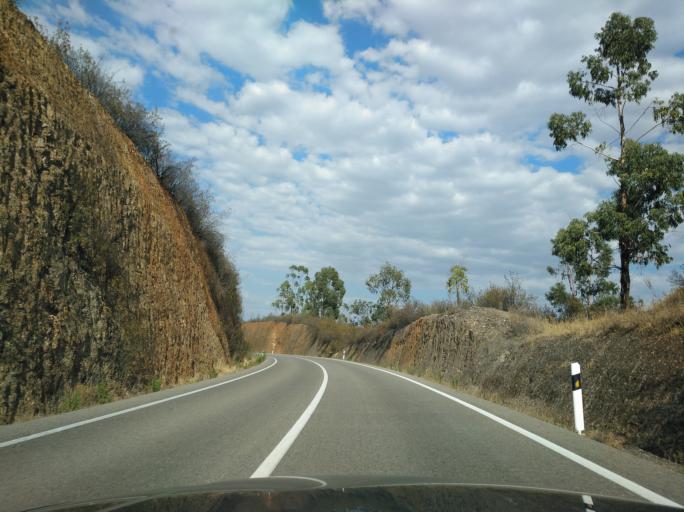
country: ES
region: Andalusia
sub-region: Provincia de Huelva
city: Rosal de la Frontera
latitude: 37.8829
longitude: -7.2046
